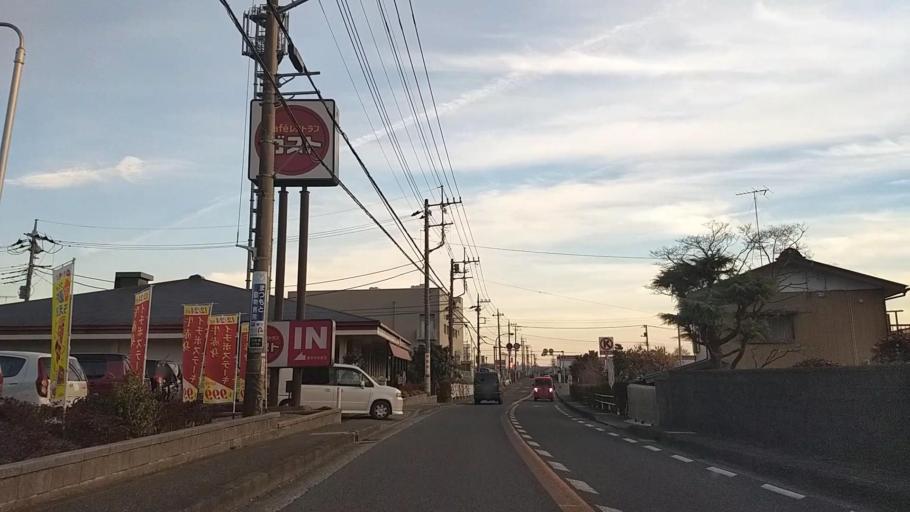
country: JP
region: Kanagawa
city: Atsugi
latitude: 35.4843
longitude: 139.3312
